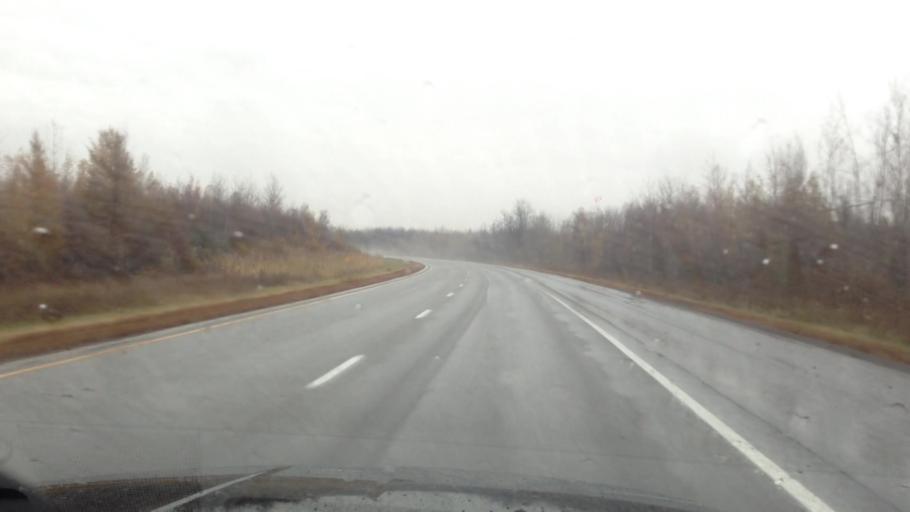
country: CA
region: Ontario
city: Casselman
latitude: 45.3065
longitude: -75.1473
